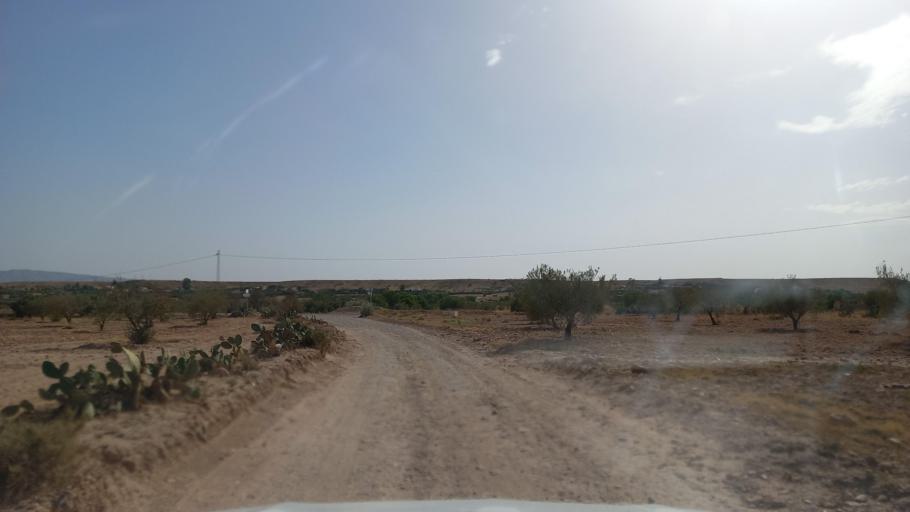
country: TN
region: Al Qasrayn
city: Kasserine
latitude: 35.2666
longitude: 8.9339
